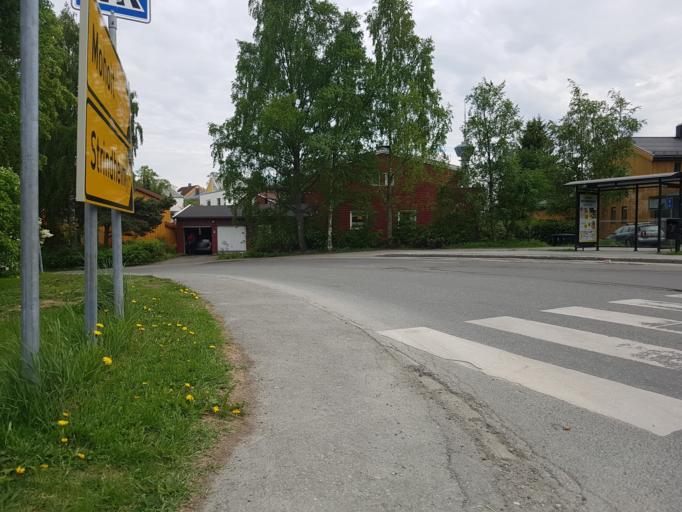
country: NO
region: Sor-Trondelag
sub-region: Trondheim
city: Trondheim
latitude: 63.4277
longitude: 10.4326
